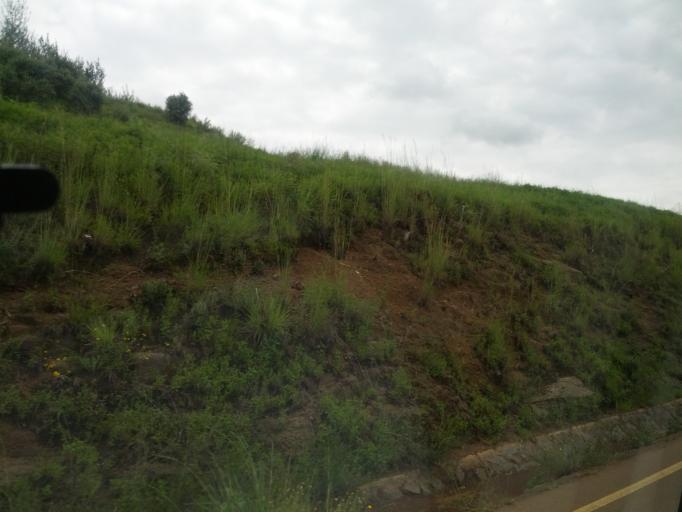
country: LS
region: Butha-Buthe
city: Butha-Buthe
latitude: -29.0338
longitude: 28.2618
